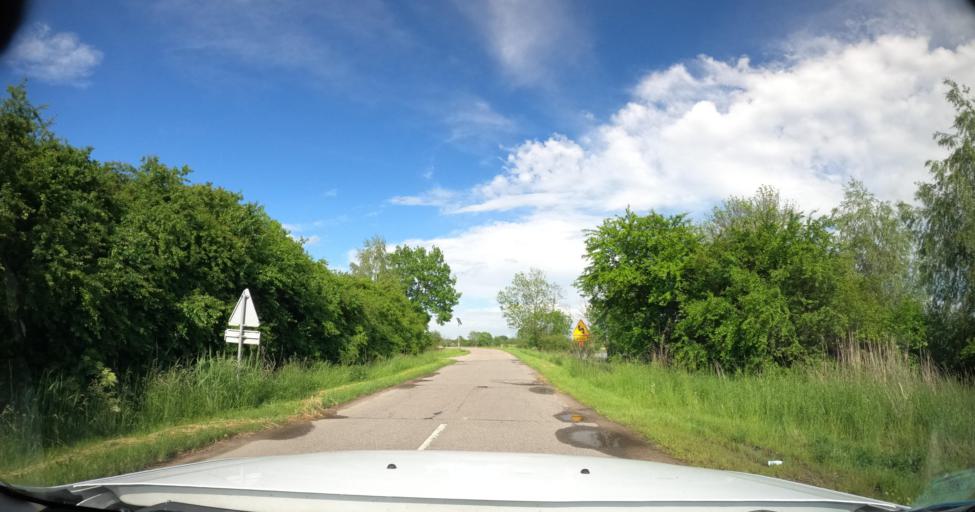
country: PL
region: Warmian-Masurian Voivodeship
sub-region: Powiat elblaski
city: Gronowo Elblaskie
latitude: 54.1723
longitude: 19.2516
